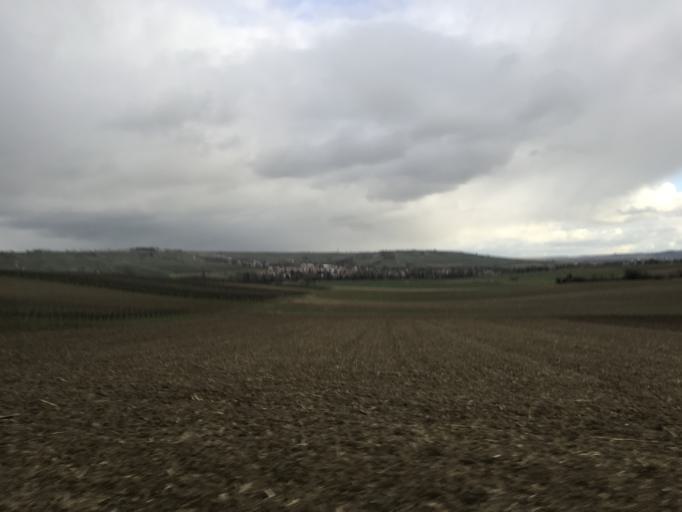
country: DE
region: Rheinland-Pfalz
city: Jugenheim
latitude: 49.9060
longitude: 8.1019
